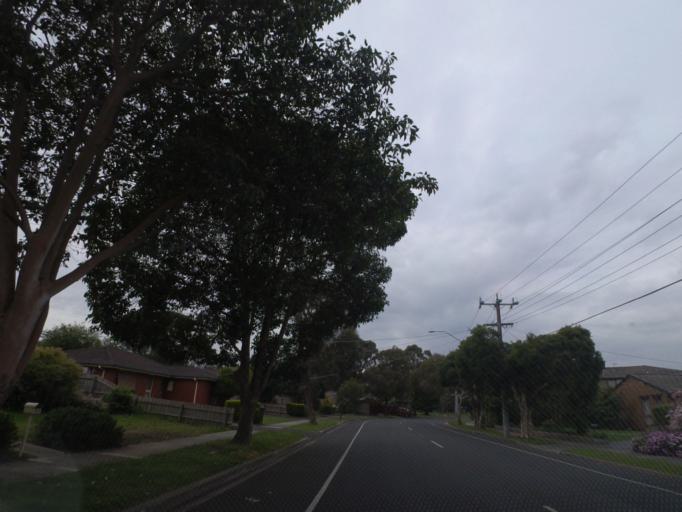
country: AU
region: Victoria
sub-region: Maroondah
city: Bayswater North
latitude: -37.8321
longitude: 145.2916
